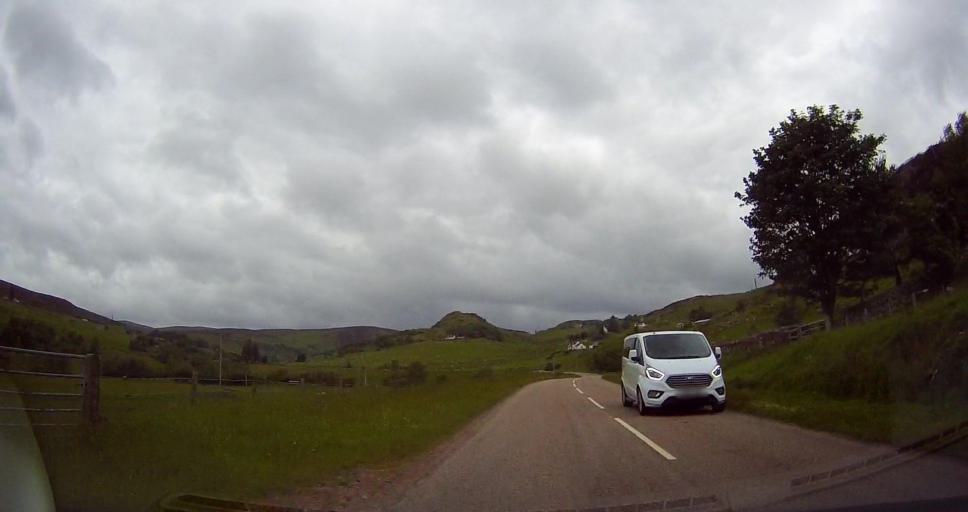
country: GB
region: Scotland
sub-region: Highland
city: Dornoch
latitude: 58.0066
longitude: -4.2398
